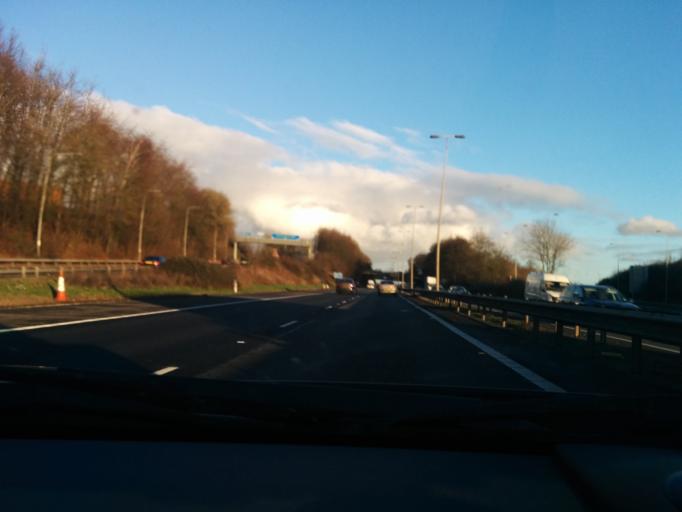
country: GB
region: England
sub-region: Buckinghamshire
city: High Wycombe
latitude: 51.6113
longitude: -0.7745
